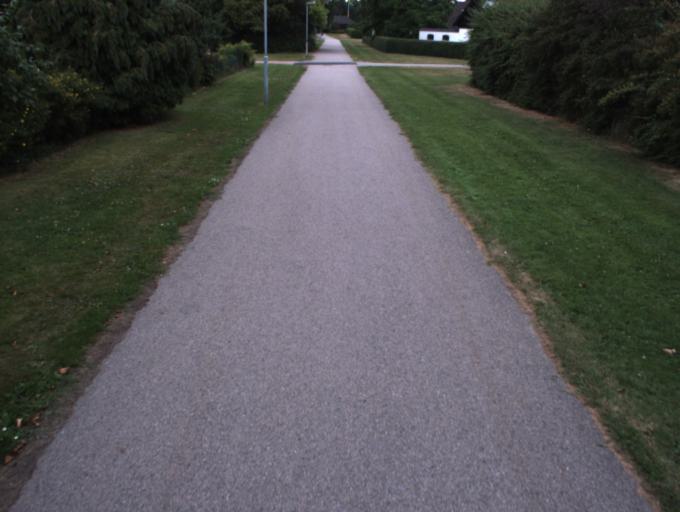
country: SE
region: Skane
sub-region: Helsingborg
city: Helsingborg
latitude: 56.0364
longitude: 12.7479
